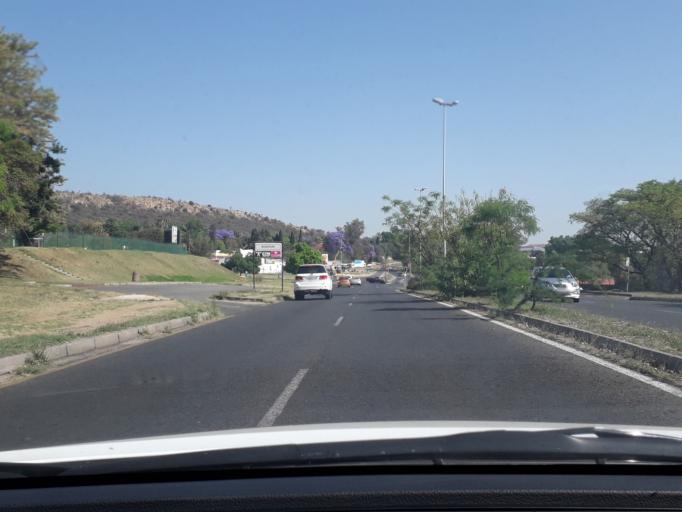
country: ZA
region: Gauteng
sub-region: City of Johannesburg Metropolitan Municipality
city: Roodepoort
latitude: -26.0930
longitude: 27.9610
